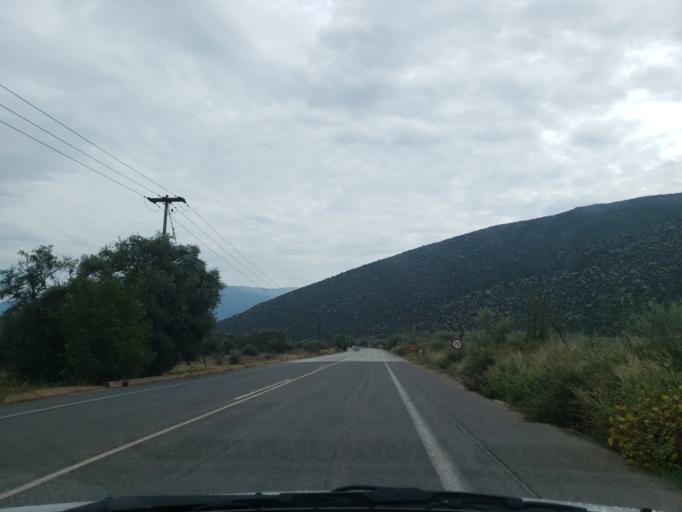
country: GR
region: Central Greece
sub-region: Nomos Fokidos
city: Itea
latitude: 38.4862
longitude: 22.4206
